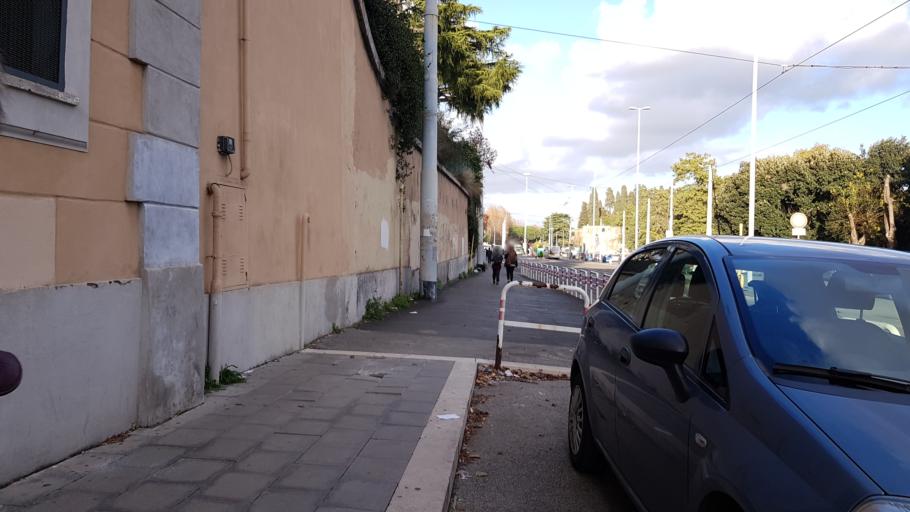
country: IT
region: Latium
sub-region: Citta metropolitana di Roma Capitale
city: Rome
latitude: 41.9004
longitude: 12.5175
